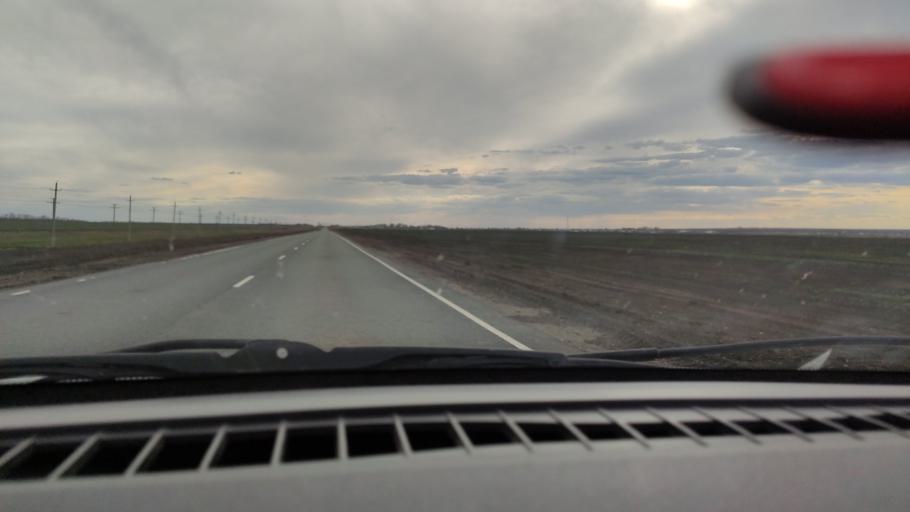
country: RU
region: Bashkortostan
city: Mayachnyy
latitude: 52.3666
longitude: 55.6073
